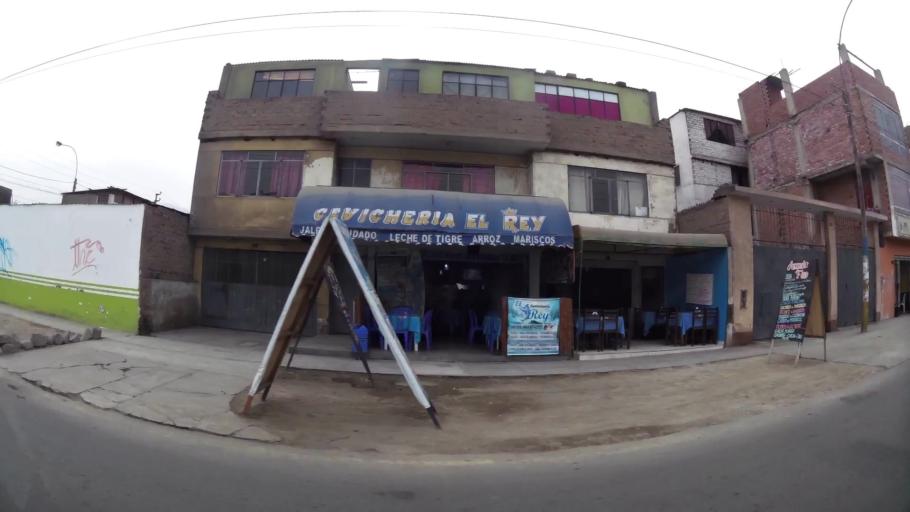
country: PE
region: Lima
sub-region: Lima
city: Independencia
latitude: -11.9744
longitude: -77.0021
